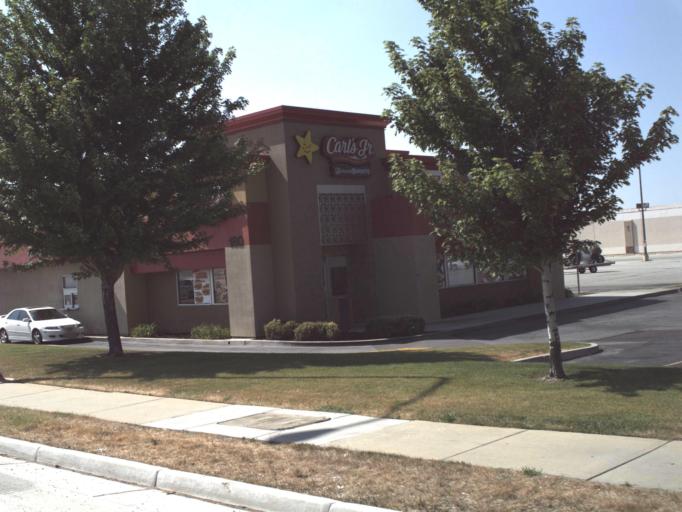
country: US
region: Utah
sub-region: Weber County
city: Ogden
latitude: 41.2444
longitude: -111.9727
